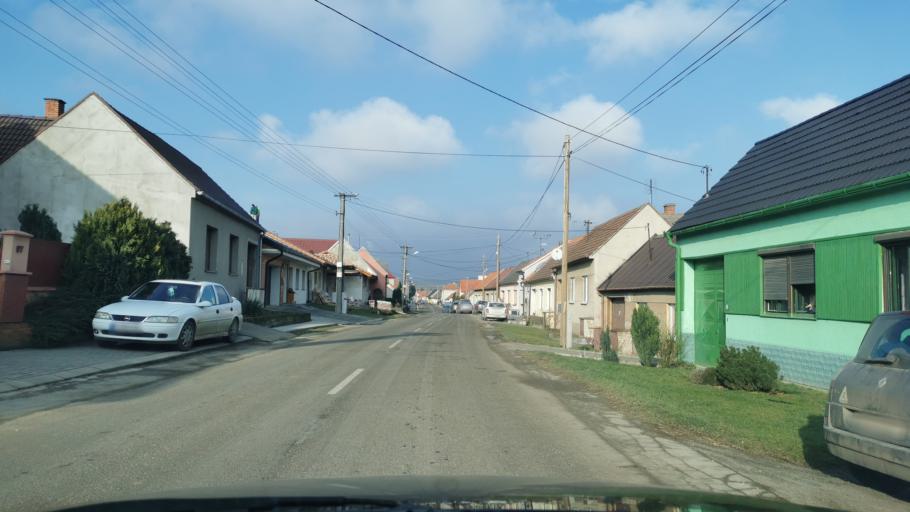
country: SK
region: Trnavsky
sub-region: Okres Skalica
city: Skalica
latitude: 48.7624
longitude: 17.2822
